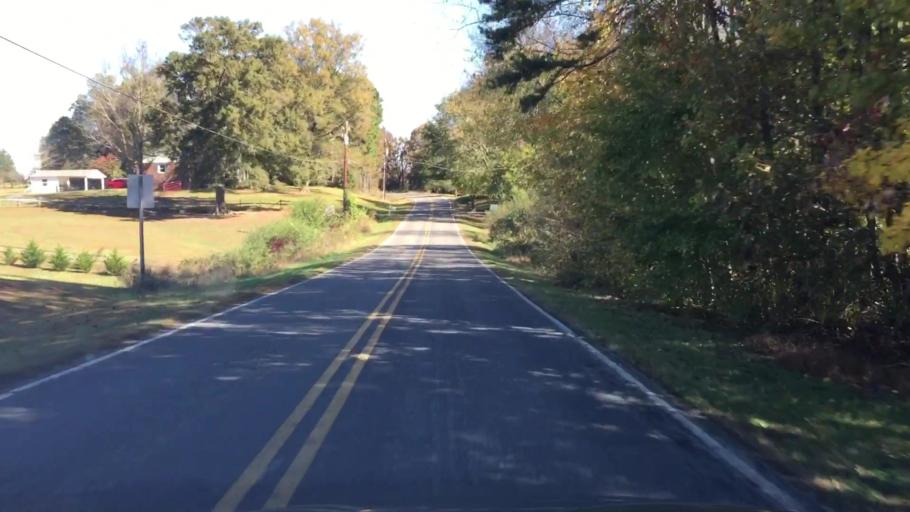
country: US
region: North Carolina
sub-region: Iredell County
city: Mooresville
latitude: 35.5870
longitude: -80.7595
